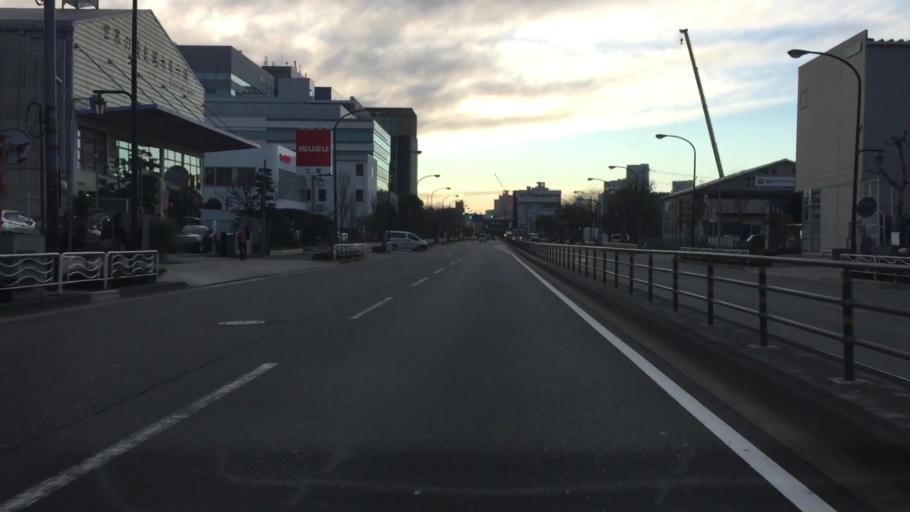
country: JP
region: Tokyo
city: Urayasu
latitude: 35.6449
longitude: 139.8293
